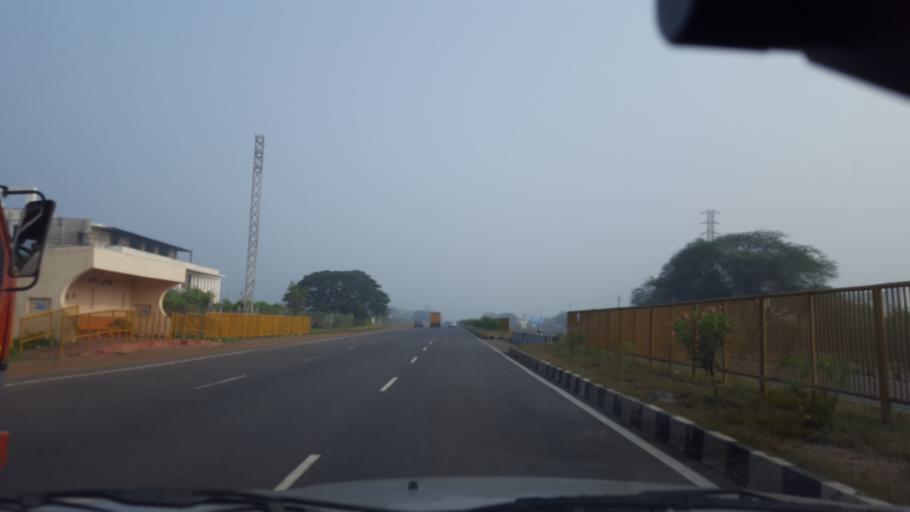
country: IN
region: Andhra Pradesh
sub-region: Prakasam
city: Ongole
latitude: 15.4316
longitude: 80.0429
